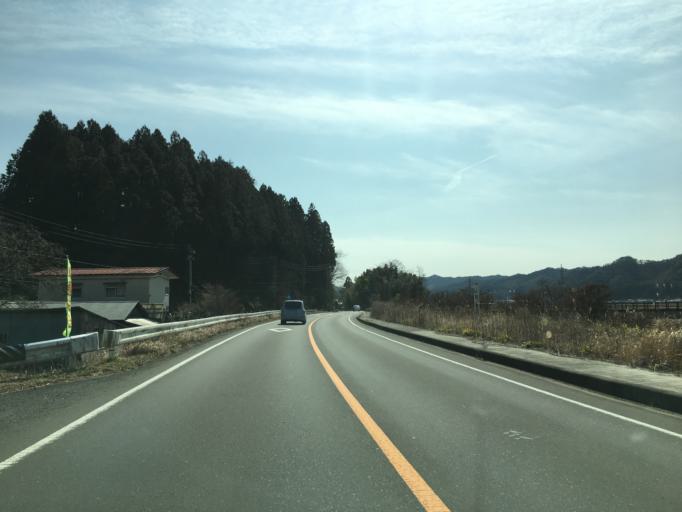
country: JP
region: Ibaraki
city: Daigo
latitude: 36.9295
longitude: 140.4153
